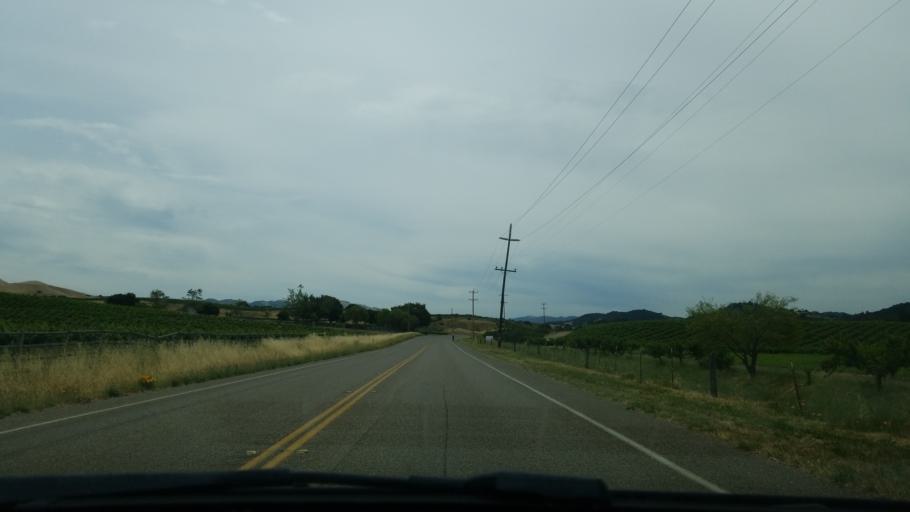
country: US
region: California
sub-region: San Luis Obispo County
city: Arroyo Grande
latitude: 35.1997
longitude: -120.5699
